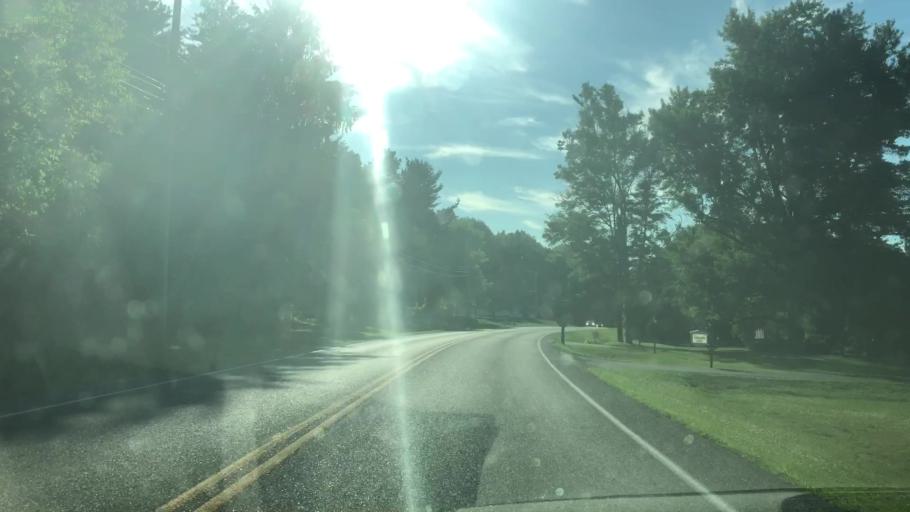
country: US
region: New York
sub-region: Ontario County
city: Victor
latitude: 43.0273
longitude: -77.4240
